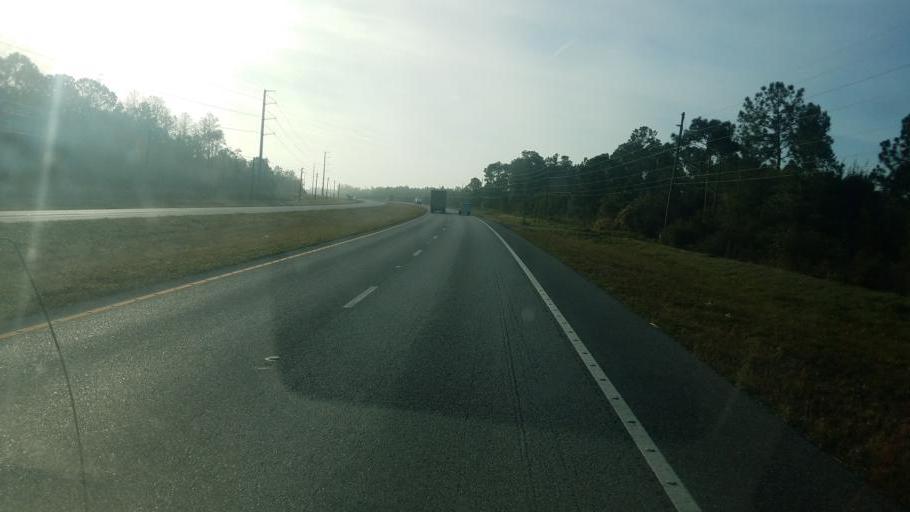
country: US
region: Florida
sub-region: Osceola County
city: Saint Cloud
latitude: 28.1718
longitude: -81.1299
